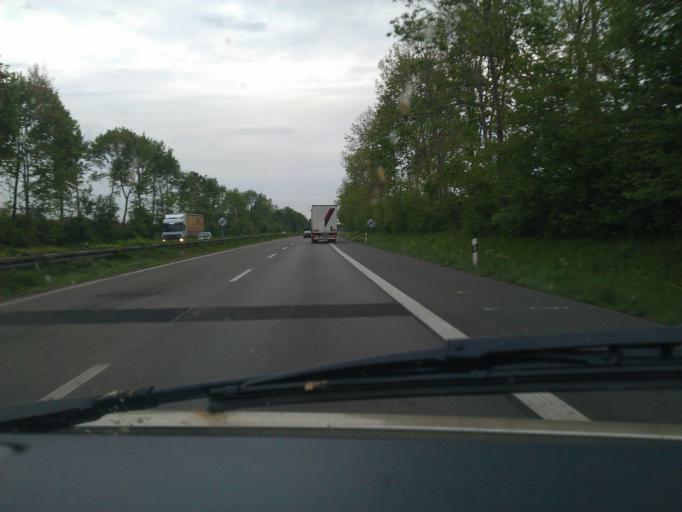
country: DE
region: North Rhine-Westphalia
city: Julich
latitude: 50.9530
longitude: 6.3516
